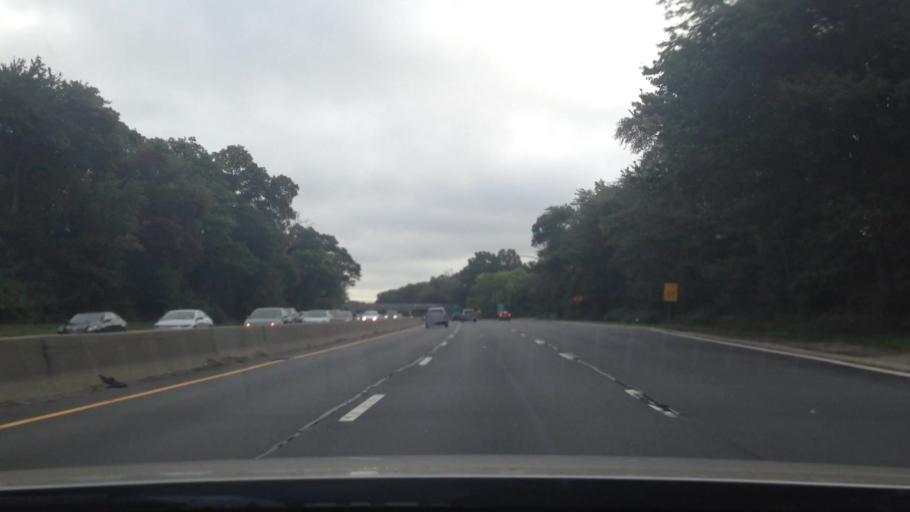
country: US
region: New York
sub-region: Suffolk County
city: North Babylon
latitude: 40.7317
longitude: -73.3254
